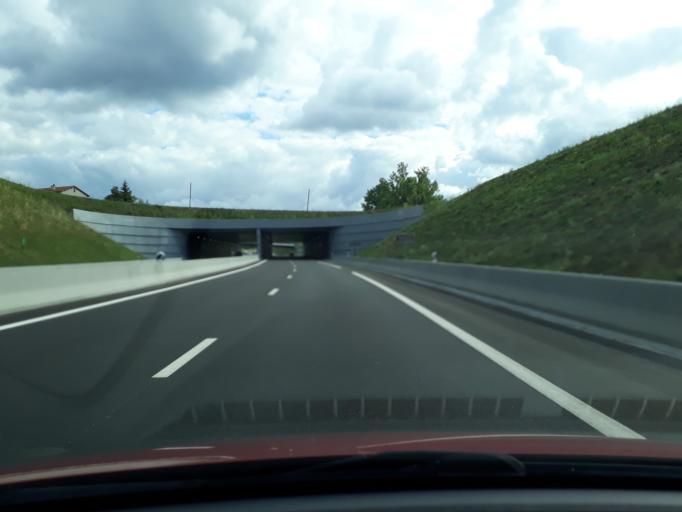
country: FR
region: Auvergne
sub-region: Departement de la Haute-Loire
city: Le Puy-en-Velay
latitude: 45.0378
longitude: 3.9075
